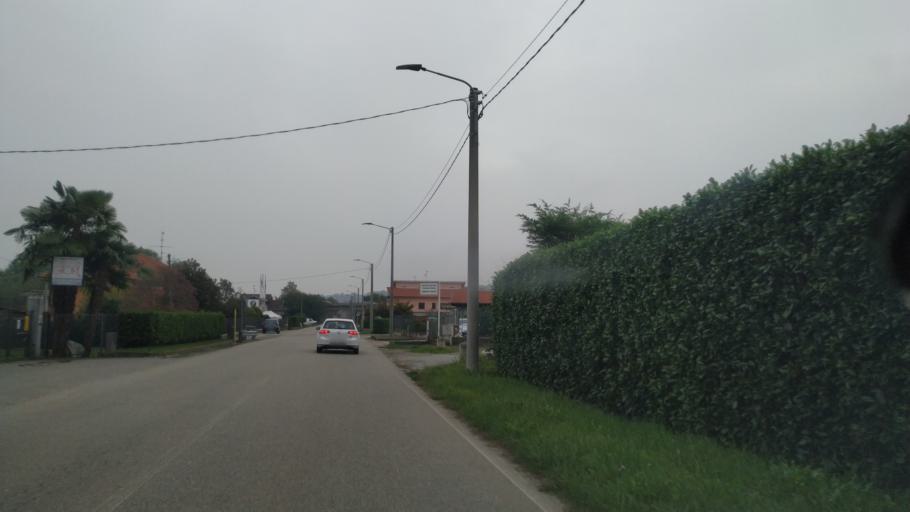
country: IT
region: Piedmont
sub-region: Provincia di Biella
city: Cerreto Castello
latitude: 45.5554
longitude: 8.1714
